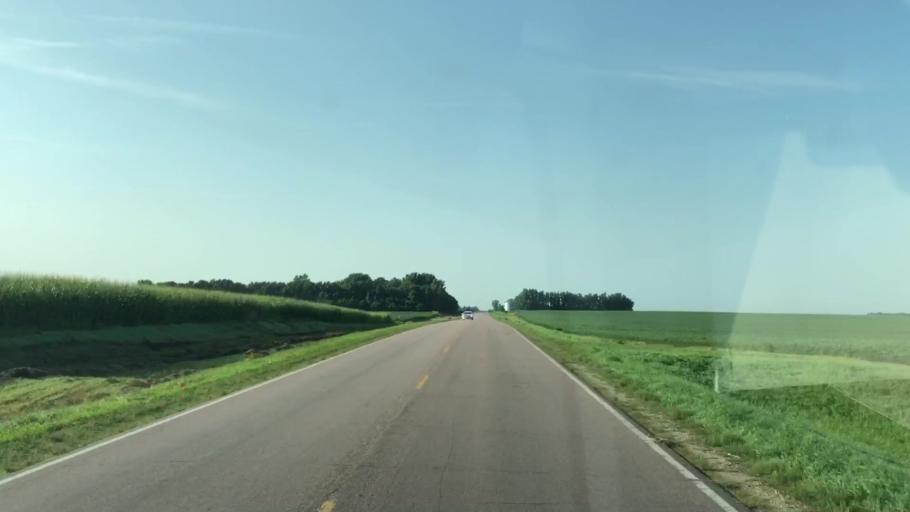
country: US
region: Iowa
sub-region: Lyon County
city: George
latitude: 43.3260
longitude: -95.9988
